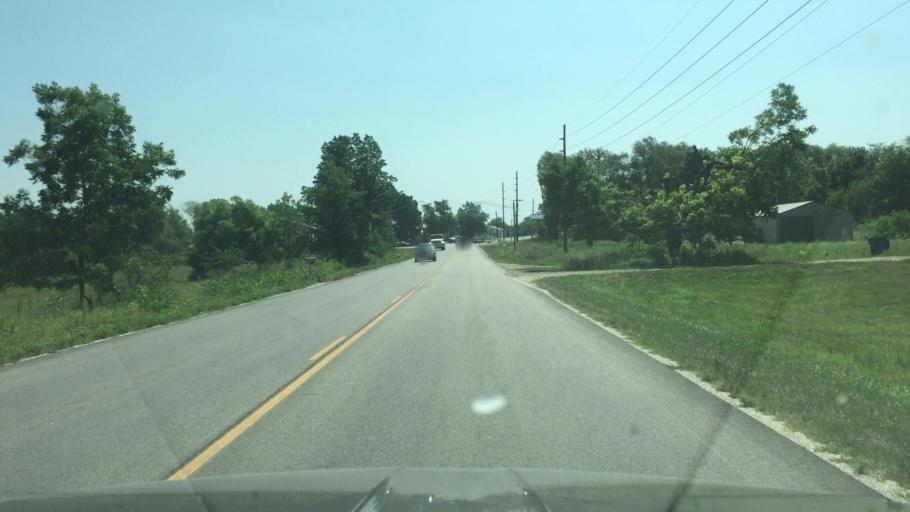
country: US
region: Missouri
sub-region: Miller County
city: Eldon
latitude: 38.3813
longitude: -92.6770
